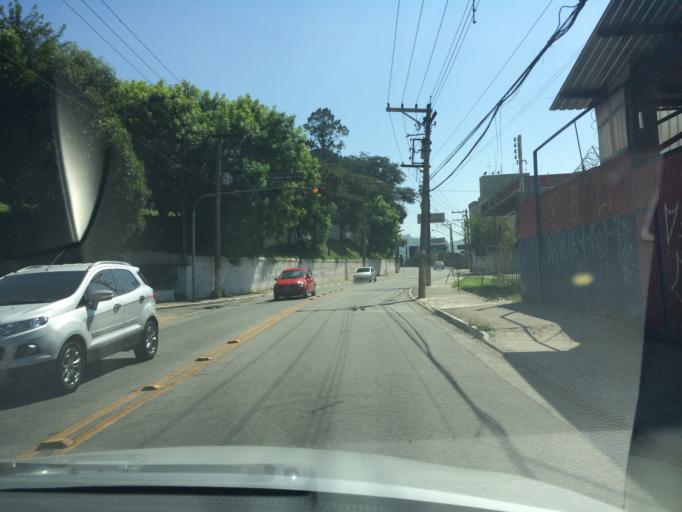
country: BR
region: Sao Paulo
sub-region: Guarulhos
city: Guarulhos
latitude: -23.4375
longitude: -46.5378
